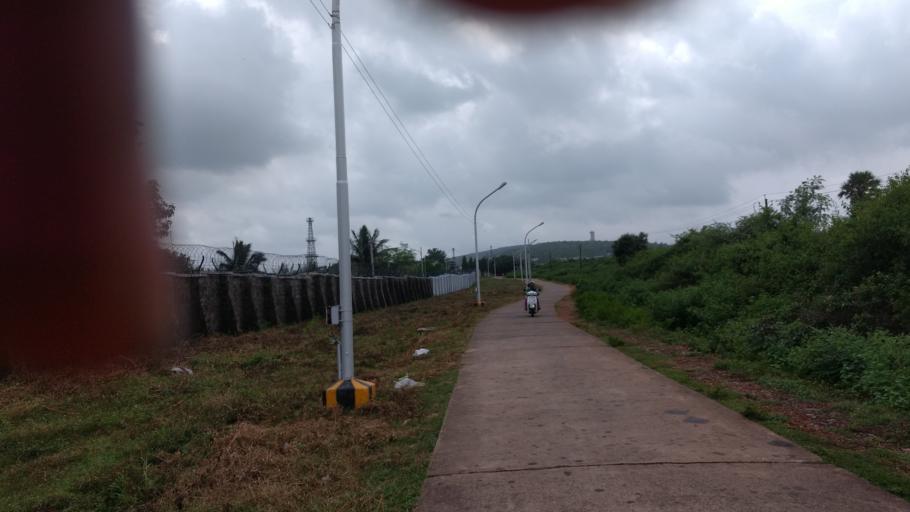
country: IN
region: Andhra Pradesh
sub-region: Vishakhapatnam
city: Yarada
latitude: 17.6734
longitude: 83.2769
